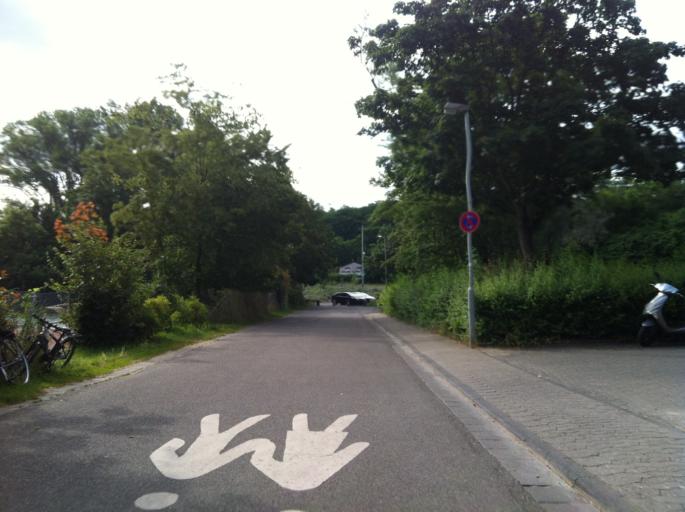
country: DE
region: Rheinland-Pfalz
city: Mainz
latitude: 50.0039
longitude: 8.2316
